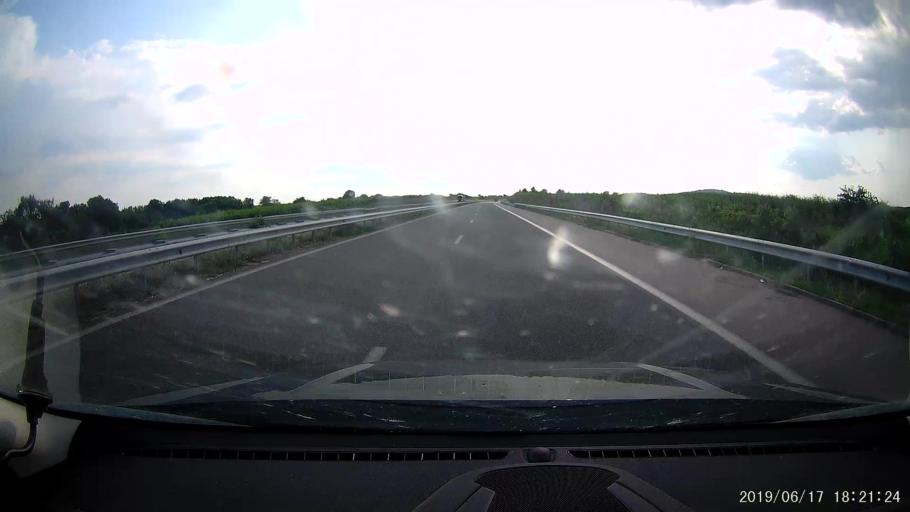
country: BG
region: Khaskovo
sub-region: Obshtina Simeonovgrad
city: Simeonovgrad
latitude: 41.9675
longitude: 25.7845
